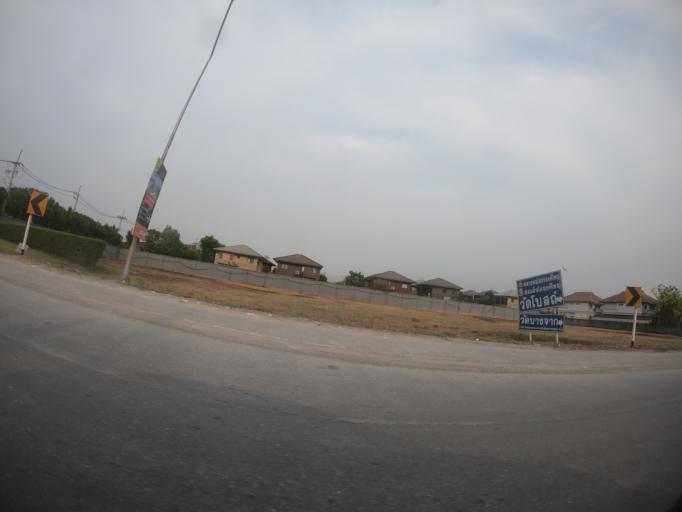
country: TH
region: Phra Nakhon Si Ayutthaya
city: Ban Bang Kadi Pathum Thani
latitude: 14.0035
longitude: 100.5717
